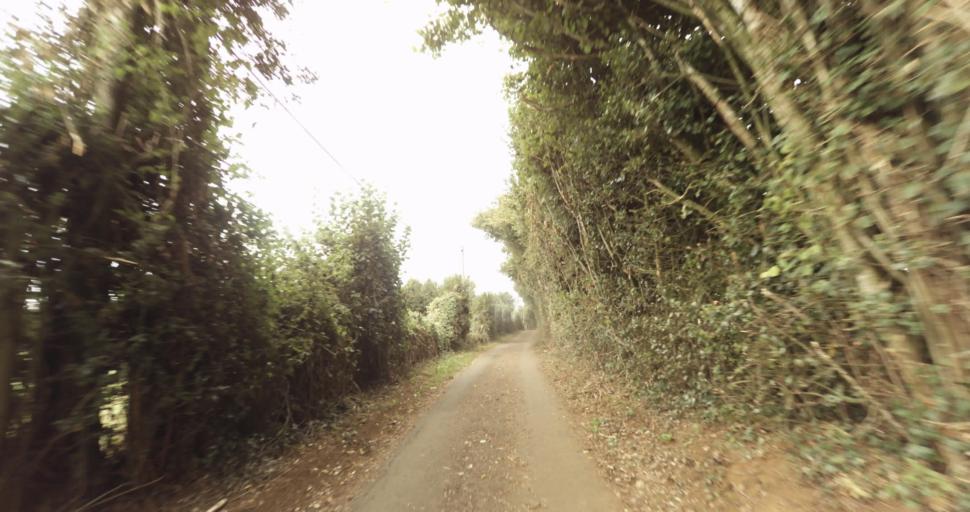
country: FR
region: Lower Normandy
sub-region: Departement de l'Orne
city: Sainte-Gauburge-Sainte-Colombe
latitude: 48.7279
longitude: 0.3726
